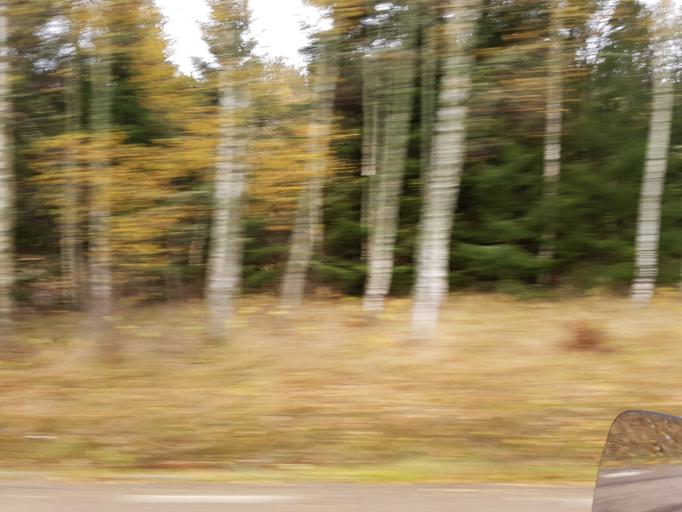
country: SE
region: Vaestra Goetaland
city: Svanesund
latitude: 58.2247
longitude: 11.8267
